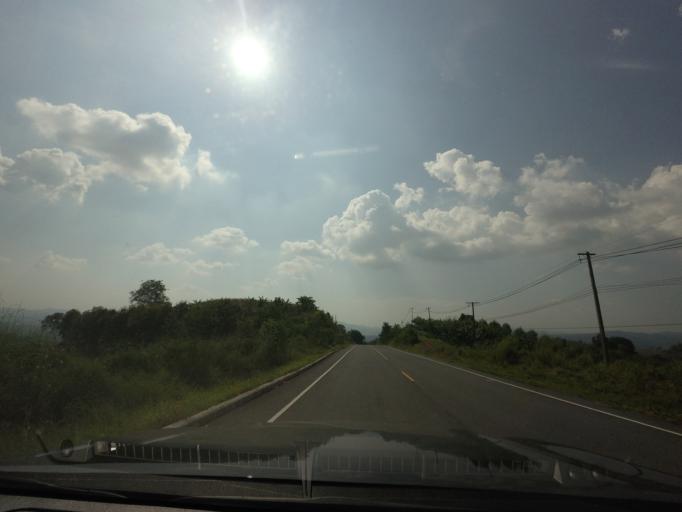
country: TH
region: Nan
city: Santi Suk
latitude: 18.9802
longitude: 100.9584
